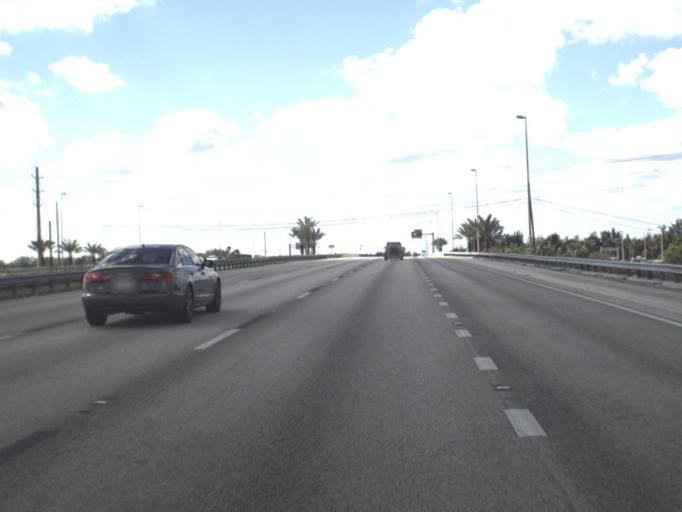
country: US
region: Florida
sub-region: Broward County
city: Parkland
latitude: 26.3003
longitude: -80.2000
